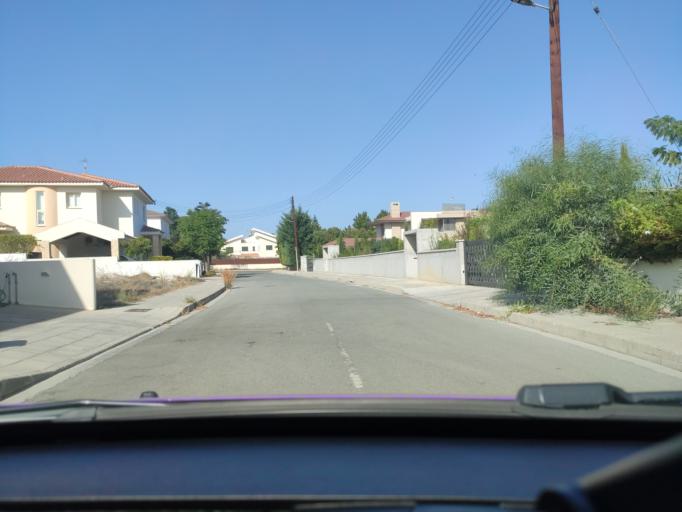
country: CY
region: Lefkosia
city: Tseri
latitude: 35.1057
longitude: 33.3554
